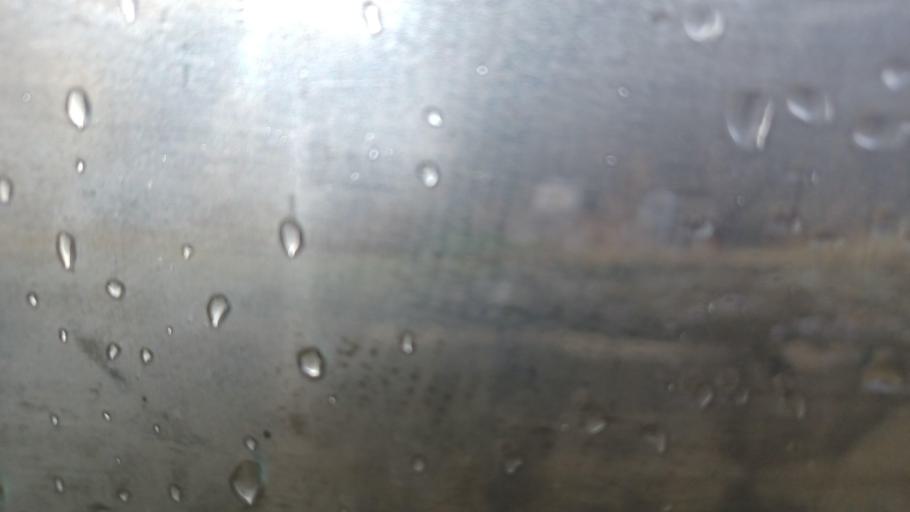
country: CY
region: Limassol
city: Kyperounta
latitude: 34.9421
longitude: 32.9606
